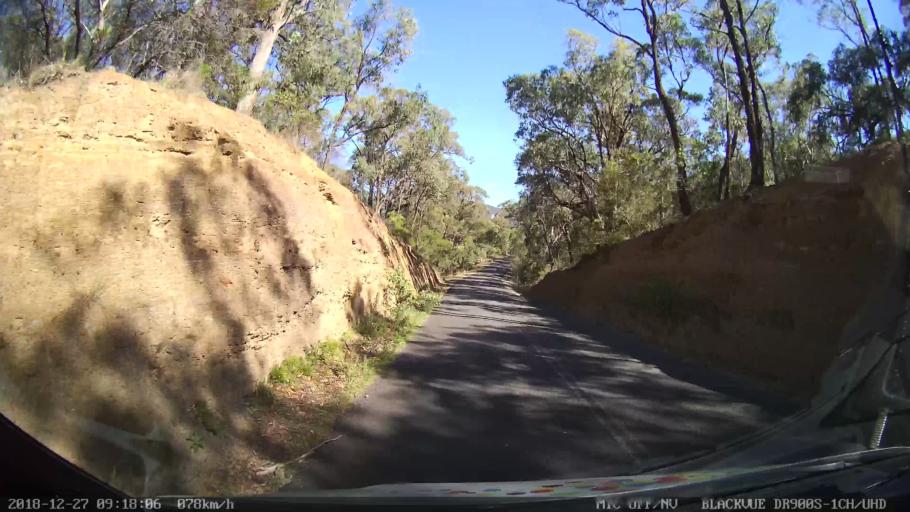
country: AU
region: New South Wales
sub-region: Lithgow
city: Portland
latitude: -33.1305
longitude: 150.0458
